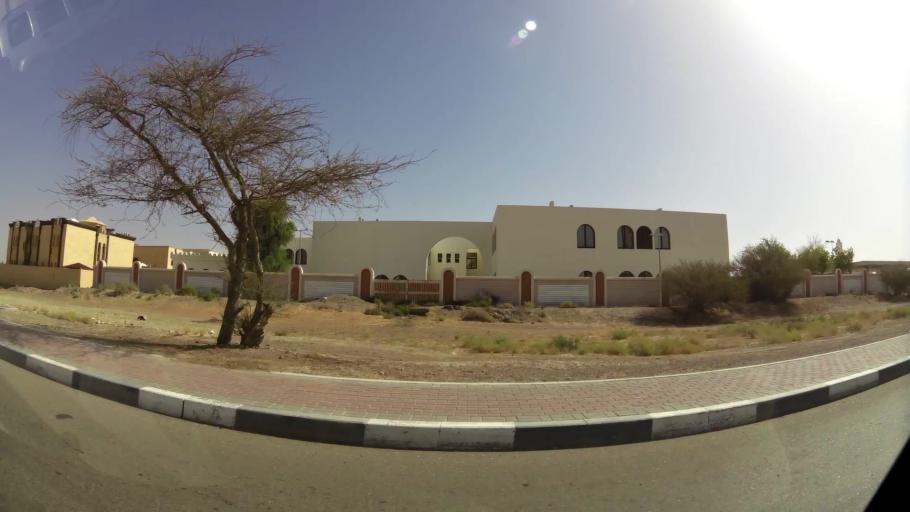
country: OM
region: Al Buraimi
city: Al Buraymi
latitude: 24.3383
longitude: 55.8014
